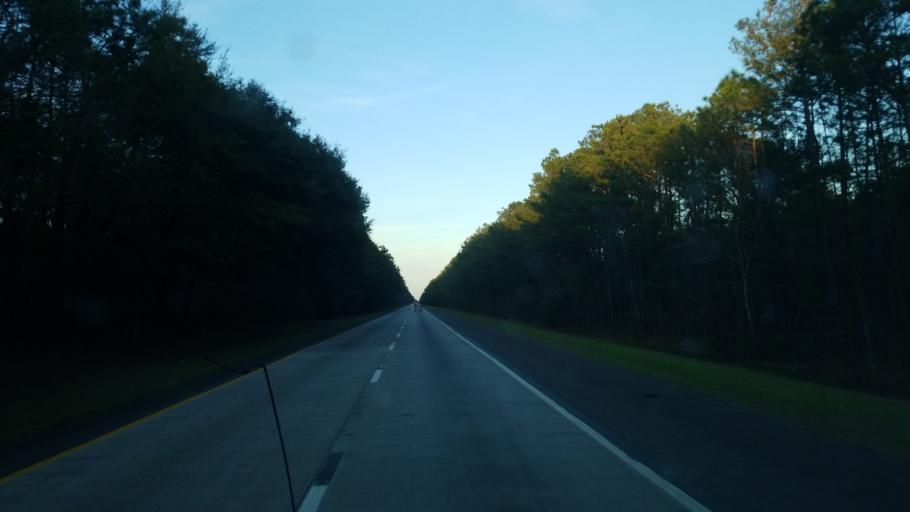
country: US
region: South Carolina
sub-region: Hampton County
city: Yemassee
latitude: 32.7679
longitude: -80.8070
